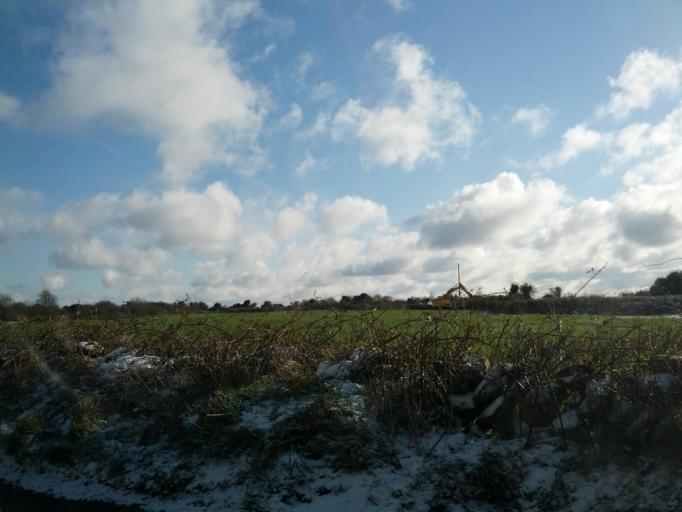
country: IE
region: Connaught
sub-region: County Galway
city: Gort
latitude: 53.1502
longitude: -8.8795
